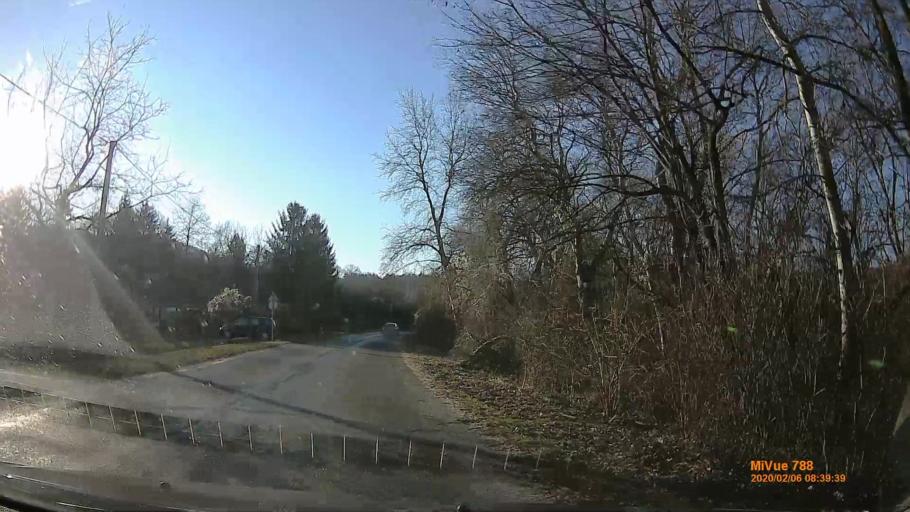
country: HU
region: Fejer
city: Szarliget
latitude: 47.5273
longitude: 18.4957
